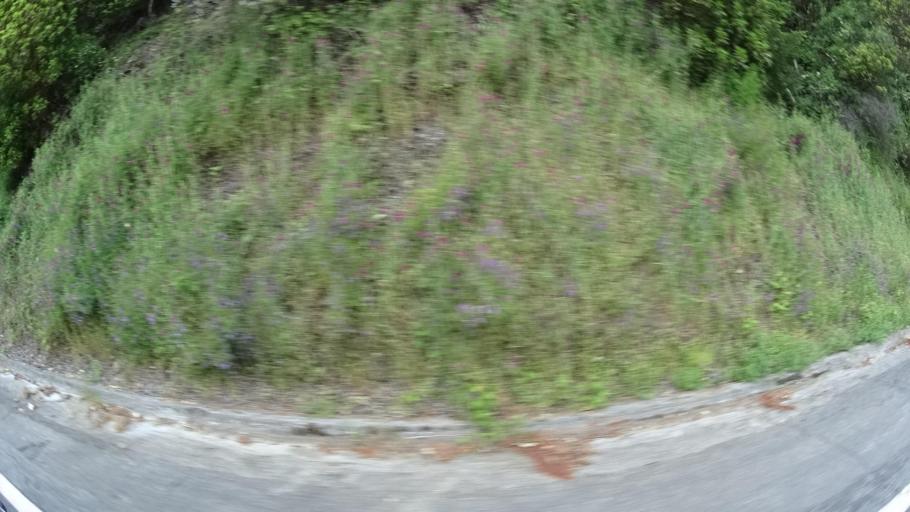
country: US
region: California
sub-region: Humboldt County
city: Willow Creek
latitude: 41.2837
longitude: -123.5763
